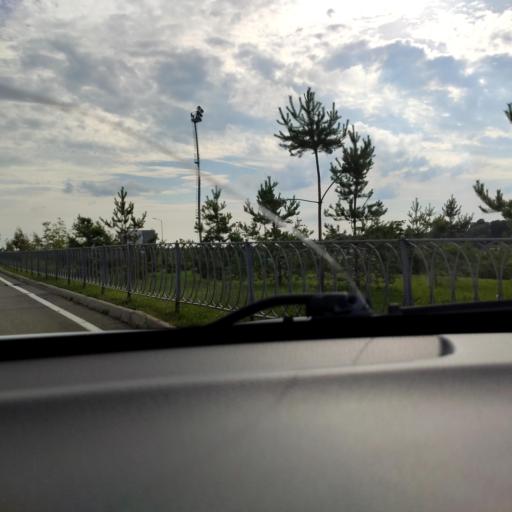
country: RU
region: Tatarstan
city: Sviyazhsk
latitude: 55.7487
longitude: 48.7411
